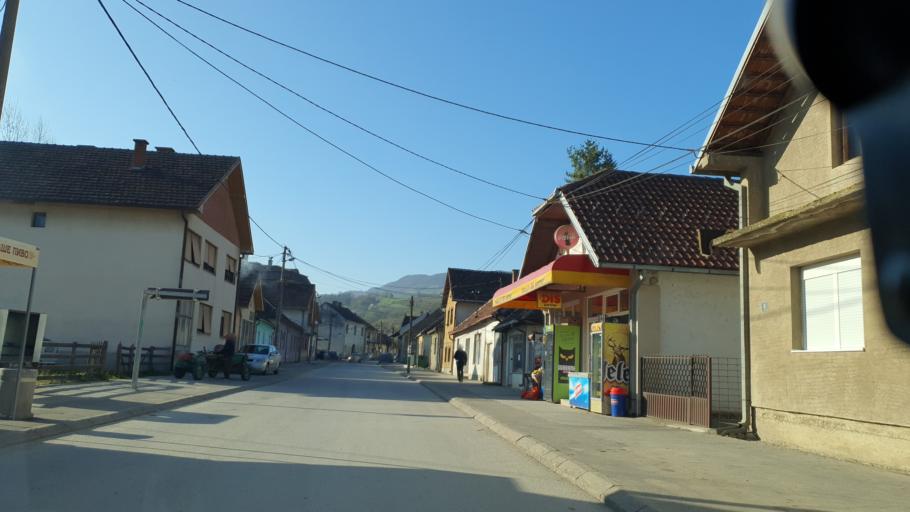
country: RS
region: Central Serbia
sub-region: Kolubarski Okrug
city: Osecina
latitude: 44.2942
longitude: 19.5394
